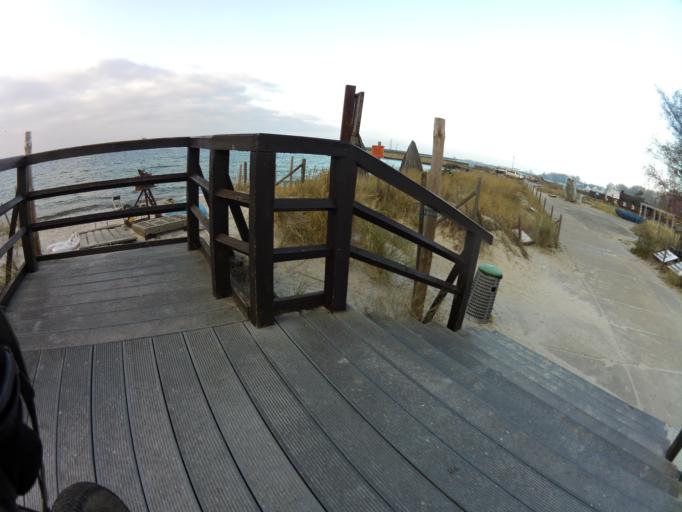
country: PL
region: Pomeranian Voivodeship
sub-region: Powiat pucki
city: Hel
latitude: 54.6084
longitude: 18.7974
